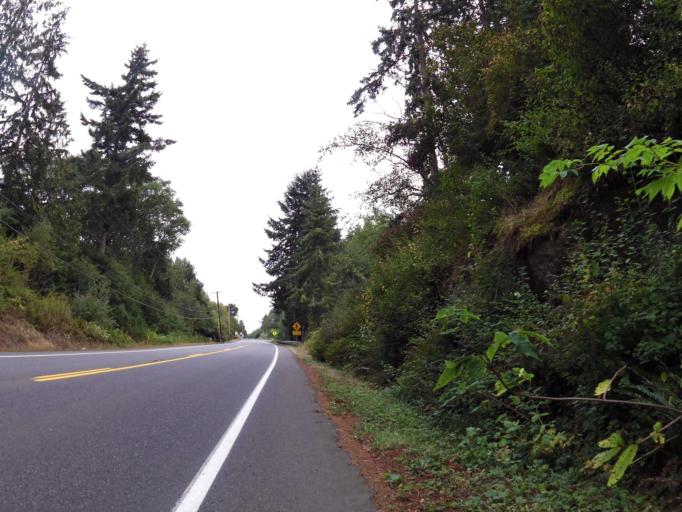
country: US
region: Washington
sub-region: Jefferson County
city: Port Ludlow
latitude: 47.9115
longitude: -122.6866
